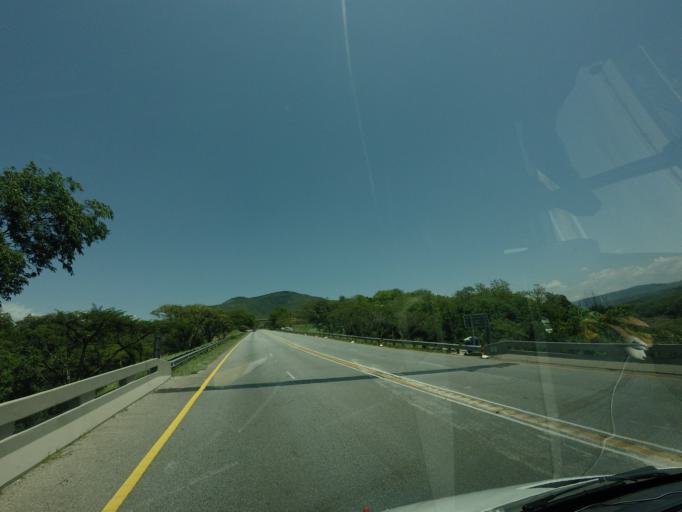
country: ZA
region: Mpumalanga
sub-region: Ehlanzeni District
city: Nelspruit
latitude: -25.4316
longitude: 30.7467
